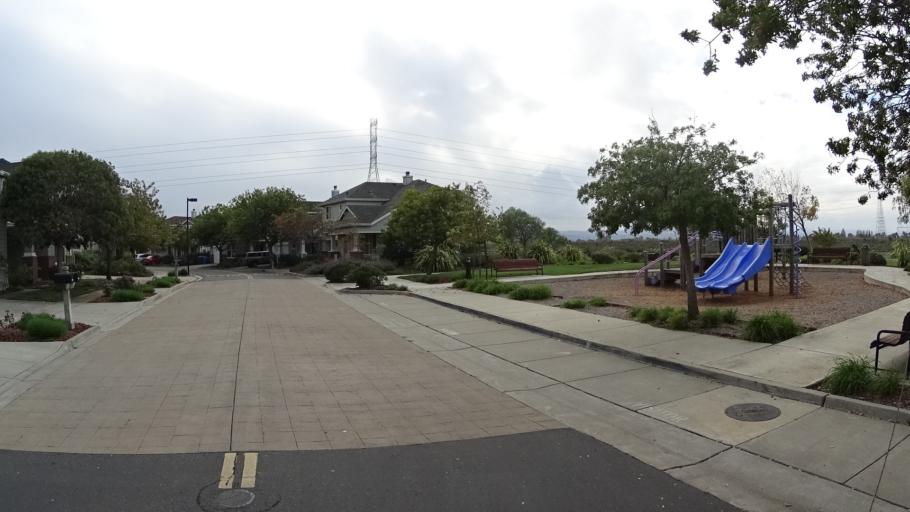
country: US
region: California
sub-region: San Mateo County
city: Redwood Shores
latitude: 37.5481
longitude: -122.2423
